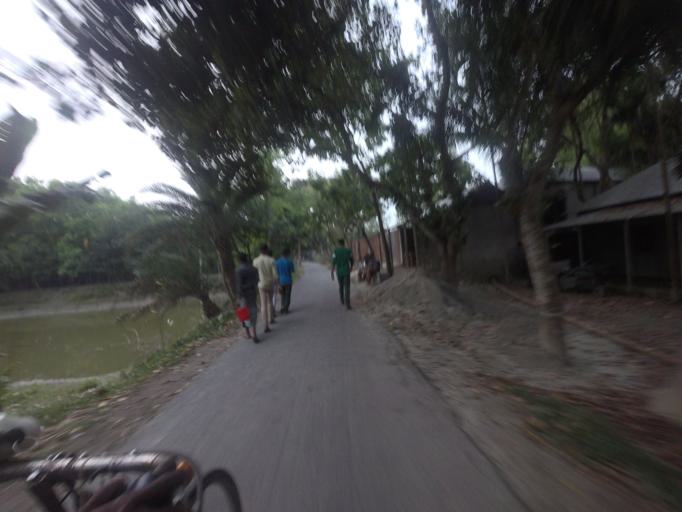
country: BD
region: Rajshahi
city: Sirajganj
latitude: 24.3174
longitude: 89.6649
